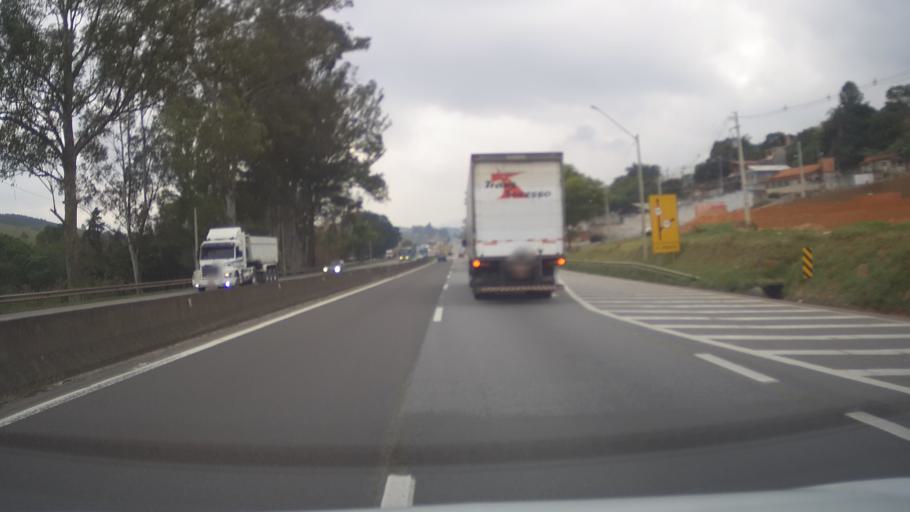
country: BR
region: Minas Gerais
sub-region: Extrema
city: Extrema
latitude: -22.8751
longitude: -46.3668
